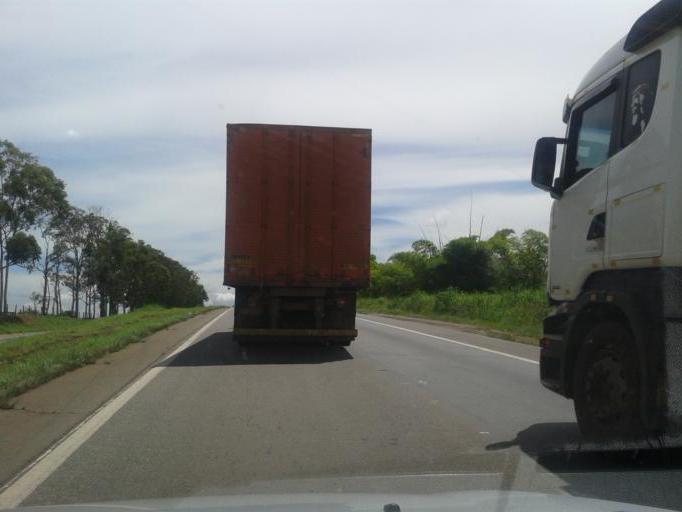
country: BR
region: Goias
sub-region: Hidrolandia
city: Hidrolandia
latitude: -16.9383
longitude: -49.2533
